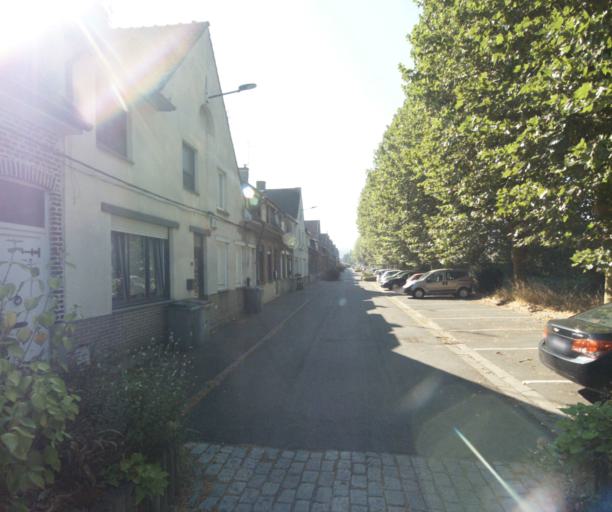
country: FR
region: Nord-Pas-de-Calais
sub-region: Departement du Nord
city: Wervicq-Sud
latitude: 50.7736
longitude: 3.0397
